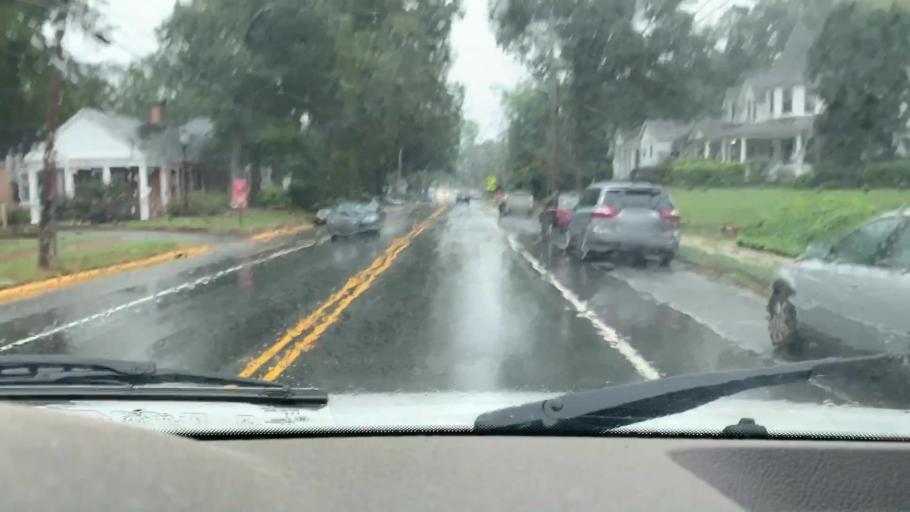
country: US
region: North Carolina
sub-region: Gaston County
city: Davidson
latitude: 35.4980
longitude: -80.8443
